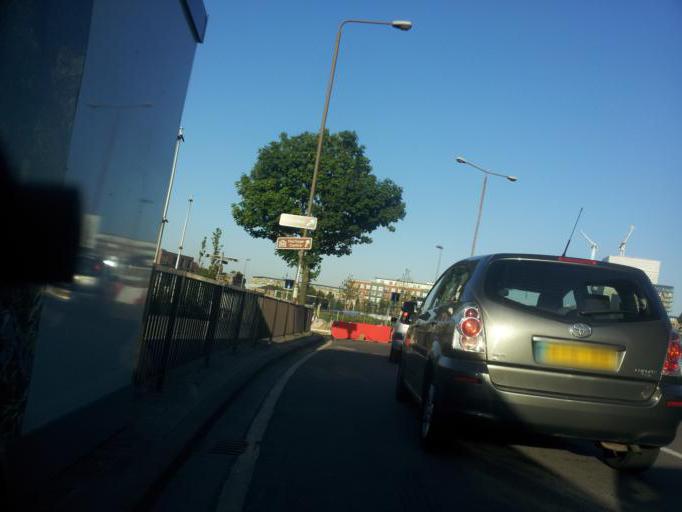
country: GB
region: England
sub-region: Greater London
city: Woolwich
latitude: 51.4938
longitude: 0.0654
